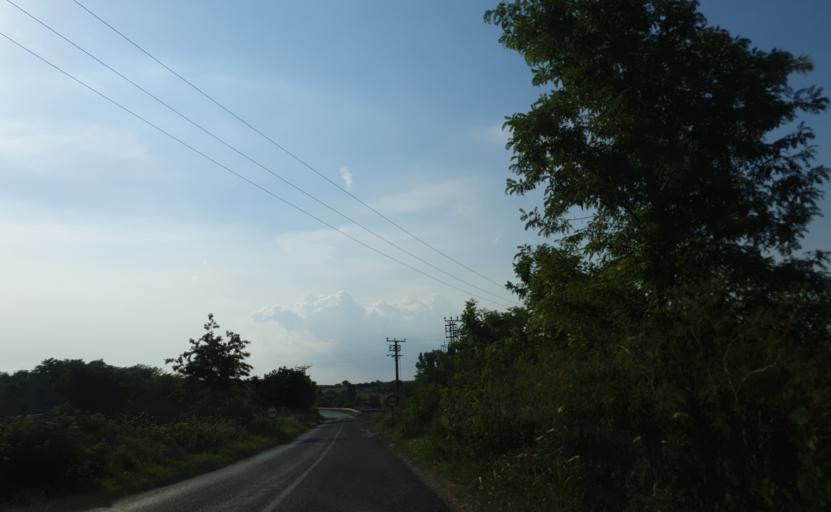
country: TR
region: Tekirdag
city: Muratli
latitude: 41.1952
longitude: 27.4727
